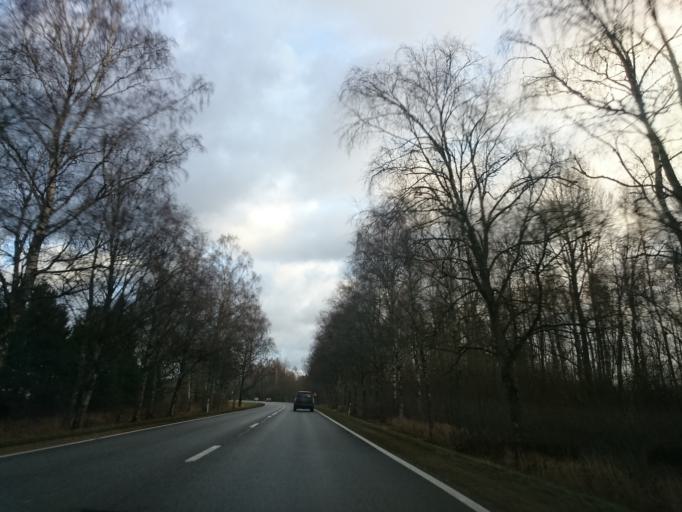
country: LV
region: Ligatne
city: Ligatne
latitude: 57.1679
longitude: 24.9646
